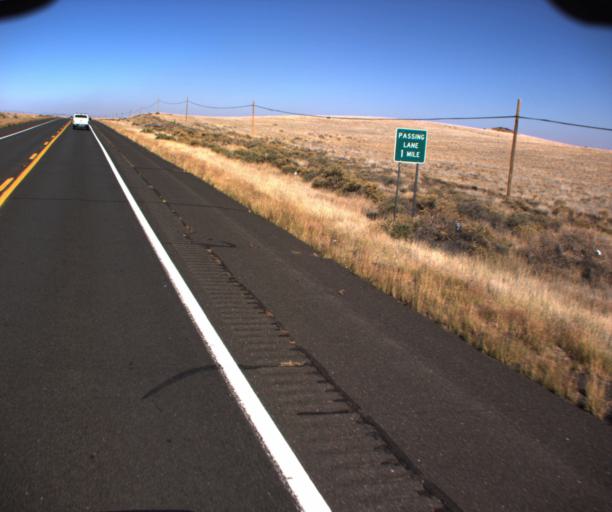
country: US
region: Arizona
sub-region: Coconino County
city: Flagstaff
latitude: 35.6078
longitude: -111.5244
